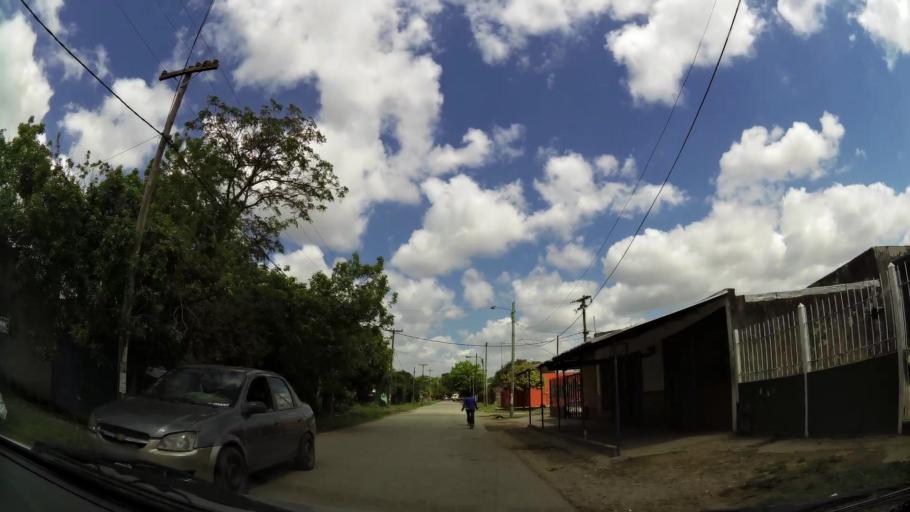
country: AR
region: Buenos Aires
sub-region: Partido de Quilmes
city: Quilmes
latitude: -34.8263
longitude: -58.2431
